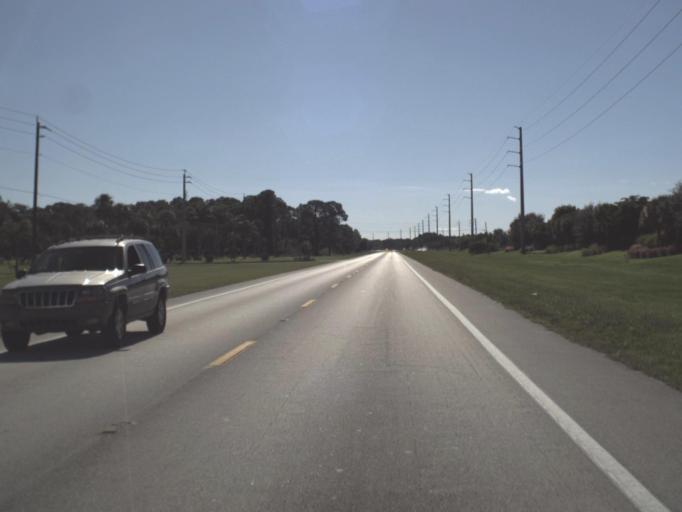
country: US
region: Florida
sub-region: Lee County
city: Gateway
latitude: 26.6009
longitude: -81.7474
